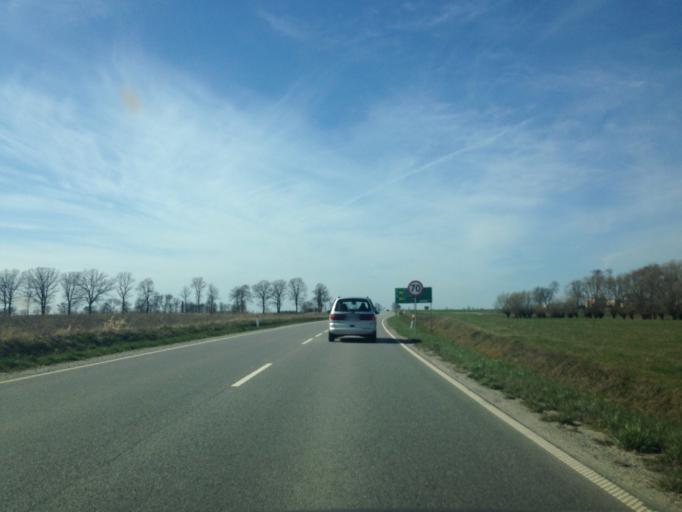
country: PL
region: Pomeranian Voivodeship
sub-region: Powiat starogardzki
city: Smetowo Graniczne
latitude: 53.7397
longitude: 18.6737
